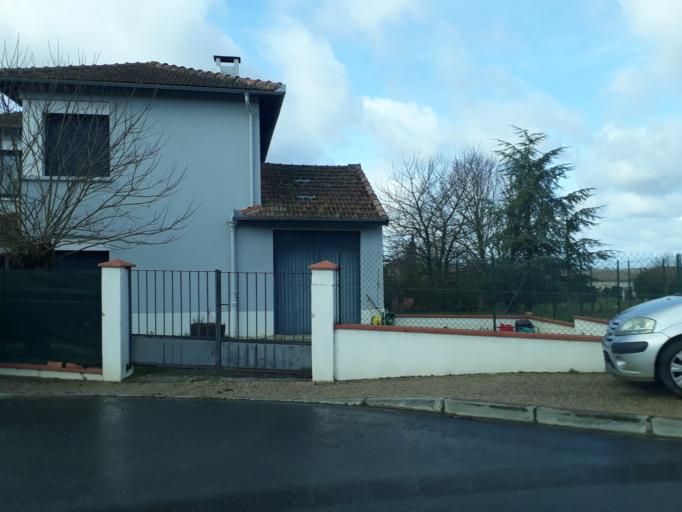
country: FR
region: Midi-Pyrenees
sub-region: Departement du Gers
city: Gimont
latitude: 43.6413
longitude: 0.9967
